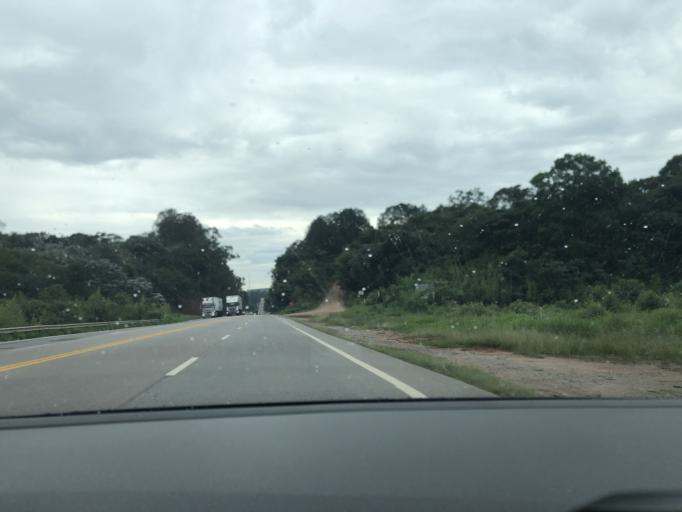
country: BR
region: Sao Paulo
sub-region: Campo Limpo Paulista
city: Campo Limpo Paulista
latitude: -23.1665
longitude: -46.7605
